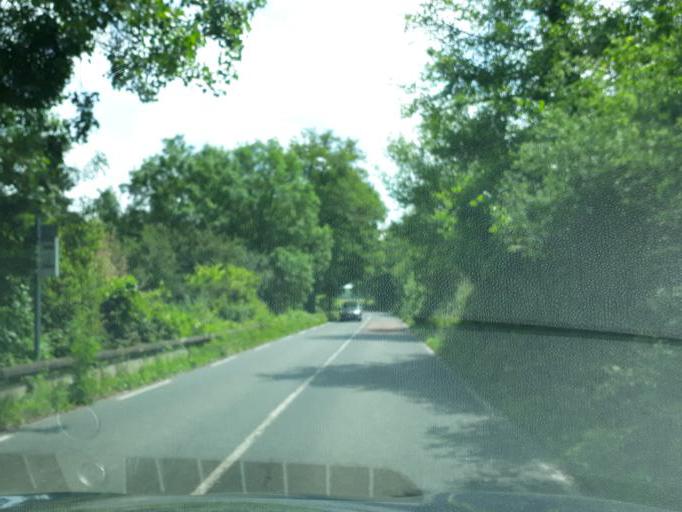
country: FR
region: Centre
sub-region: Departement du Loiret
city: Sandillon
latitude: 47.8094
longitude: 2.0549
